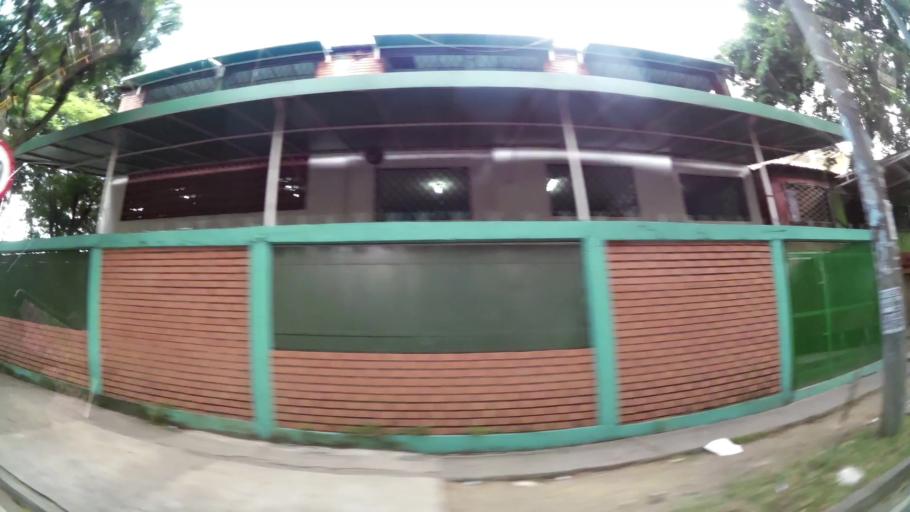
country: CO
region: Valle del Cauca
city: Cali
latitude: 3.4676
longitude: -76.4952
